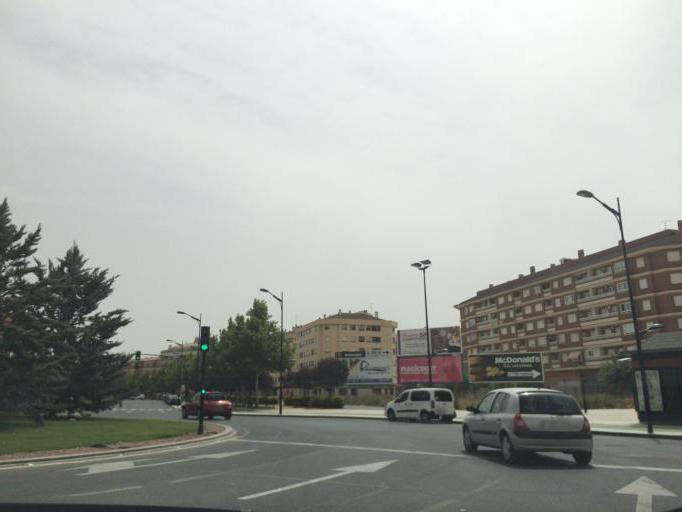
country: ES
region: Castille-La Mancha
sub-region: Provincia de Albacete
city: Albacete
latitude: 38.9874
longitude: -1.8666
